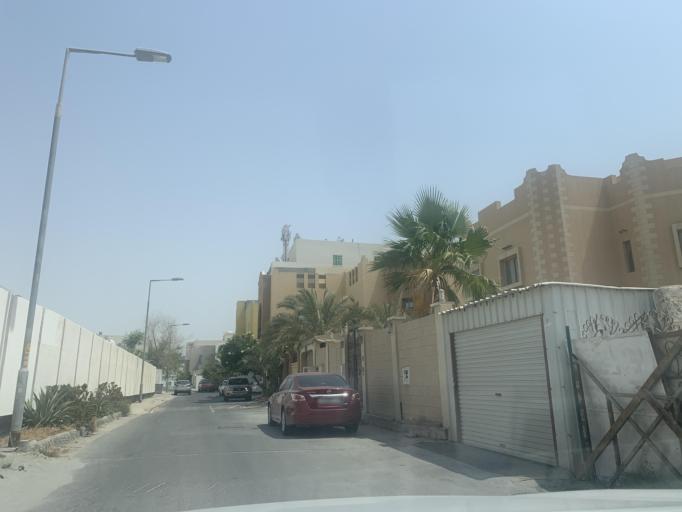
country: BH
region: Manama
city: Jidd Hafs
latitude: 26.2245
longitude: 50.4674
